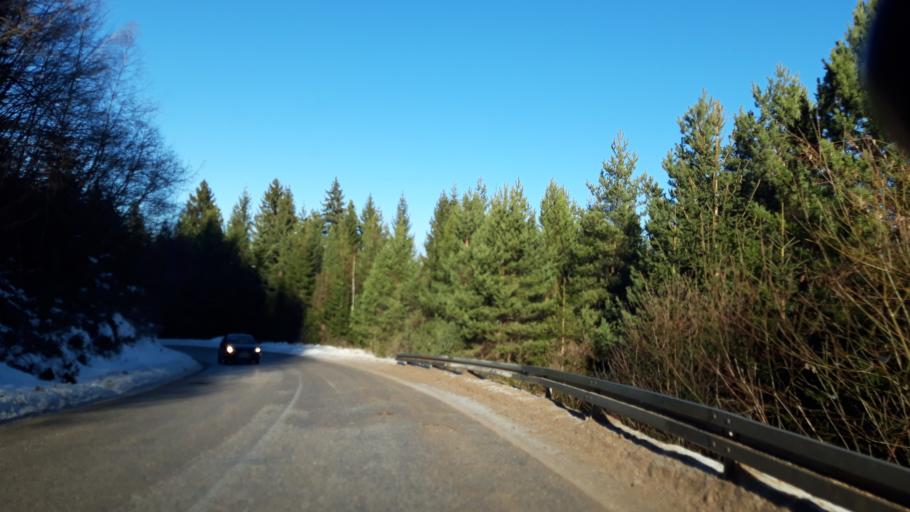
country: BA
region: Republika Srpska
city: Koran
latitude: 43.7972
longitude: 18.5553
